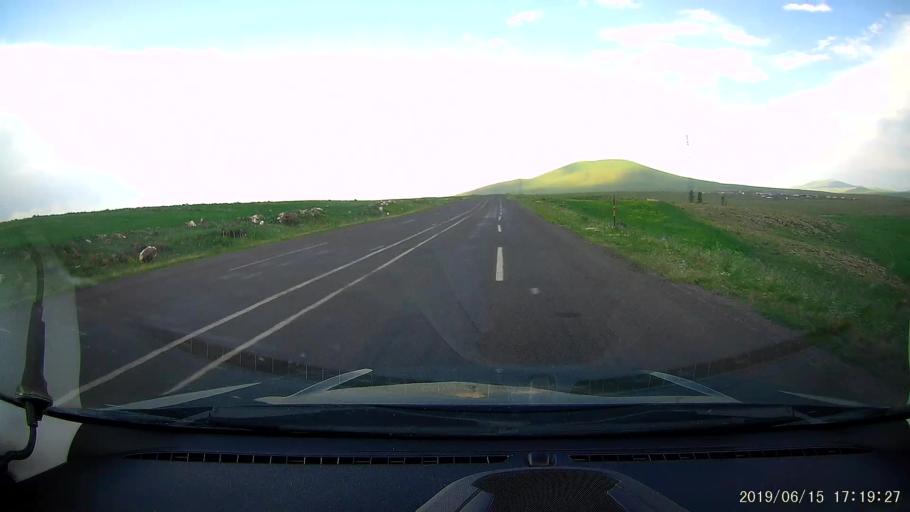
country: TR
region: Kars
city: Kars
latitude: 40.6168
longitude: 43.2787
